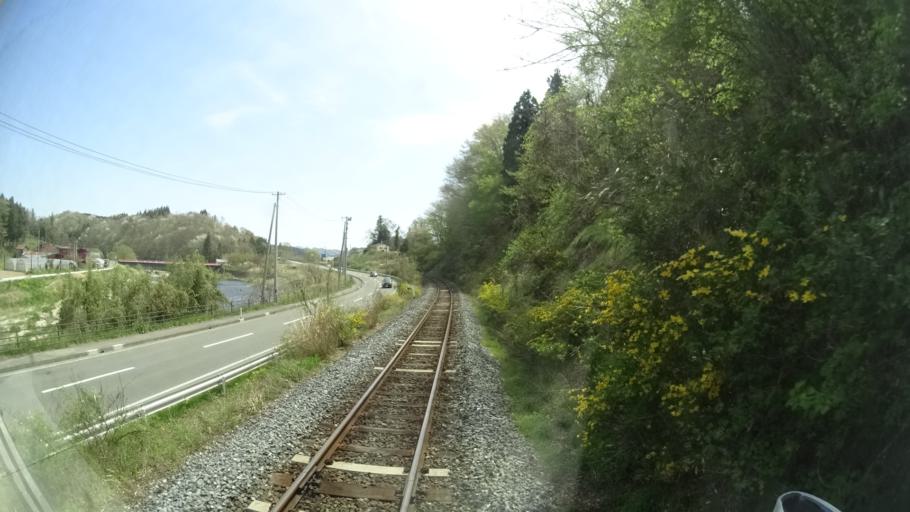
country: JP
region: Iwate
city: Ichinoseki
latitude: 38.9933
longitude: 141.3047
